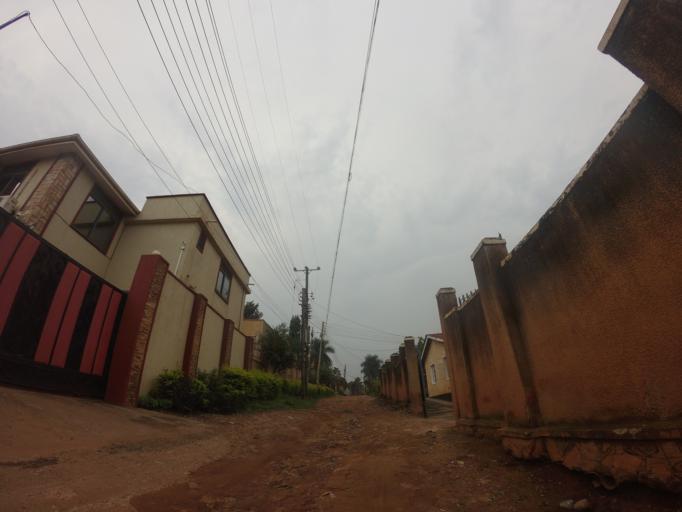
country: UG
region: Central Region
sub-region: Wakiso District
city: Kireka
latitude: 0.3422
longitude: 32.6192
